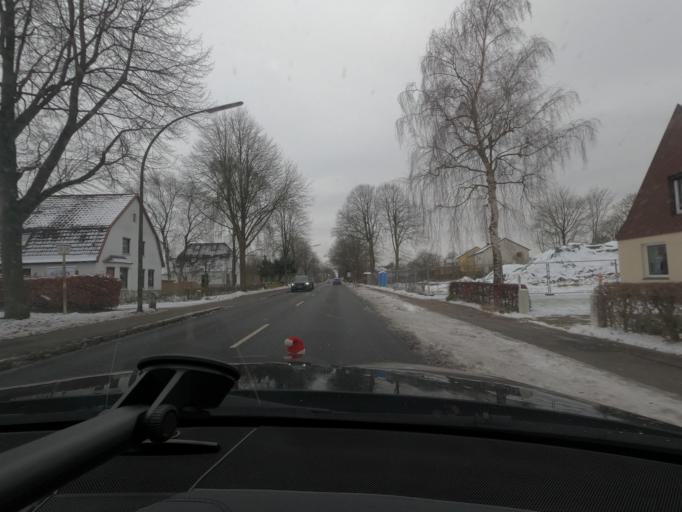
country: DE
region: Schleswig-Holstein
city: Jarplund-Weding
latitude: 54.7579
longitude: 9.4060
